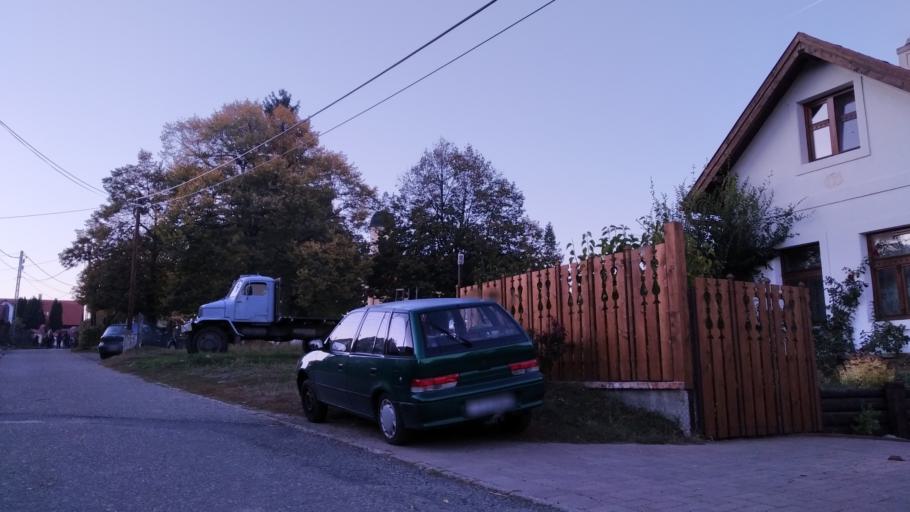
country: HU
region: Pest
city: Visegrad
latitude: 47.7261
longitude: 18.9849
